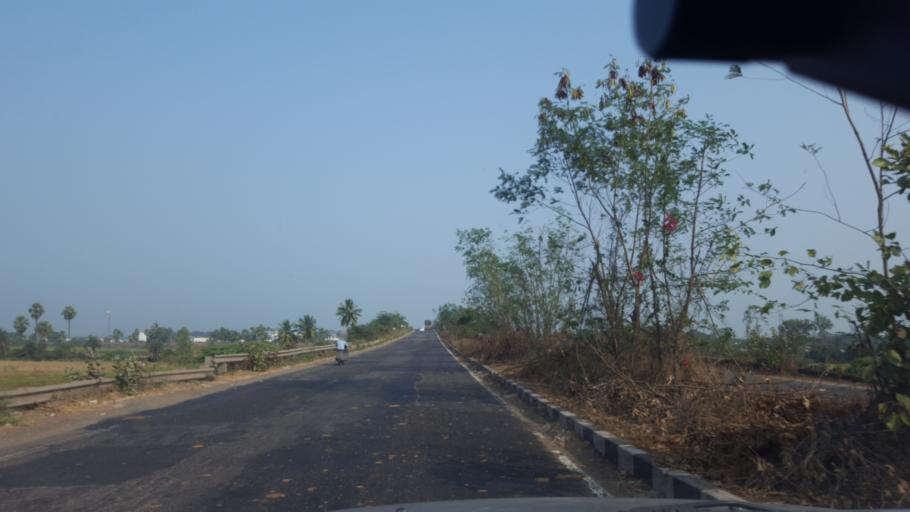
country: IN
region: Andhra Pradesh
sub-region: West Godavari
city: Eluru
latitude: 16.7374
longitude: 81.1319
